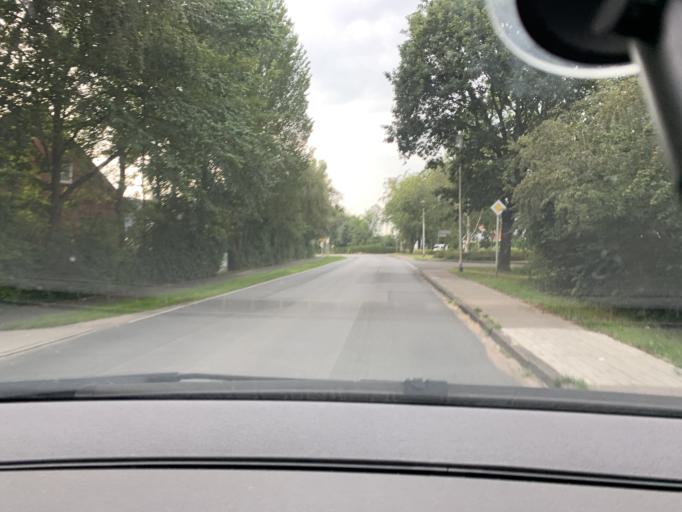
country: DE
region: Schleswig-Holstein
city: Mildstedt
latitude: 54.4660
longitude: 9.0929
